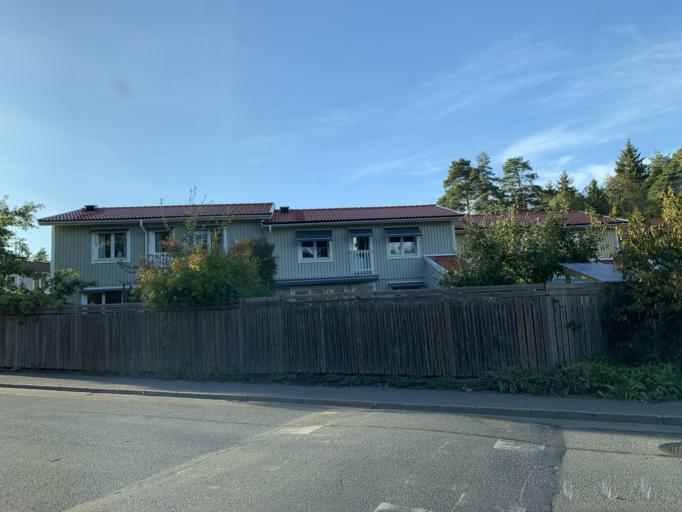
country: SE
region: Stockholm
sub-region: Taby Kommun
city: Taby
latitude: 59.4396
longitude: 18.0158
